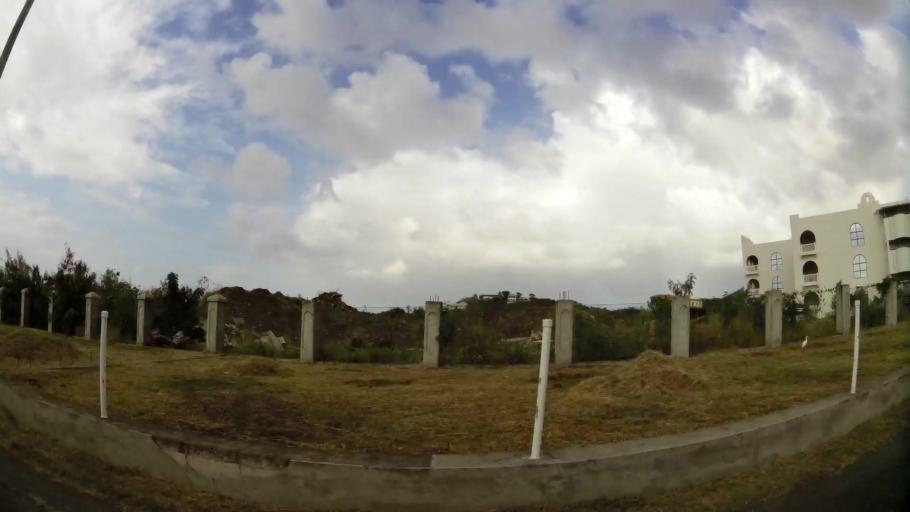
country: KN
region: Saint Thomas Lowland
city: Cotton Ground
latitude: 17.1873
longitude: -62.6185
